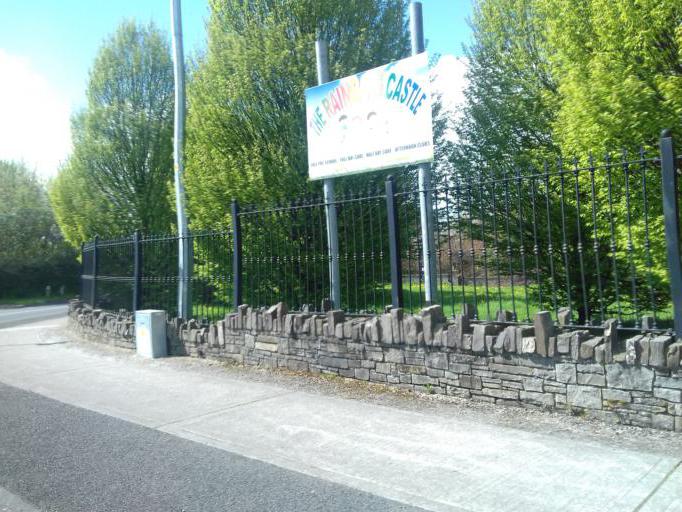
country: IE
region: Leinster
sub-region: Laois
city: Portlaoise
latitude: 53.0389
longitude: -7.2992
